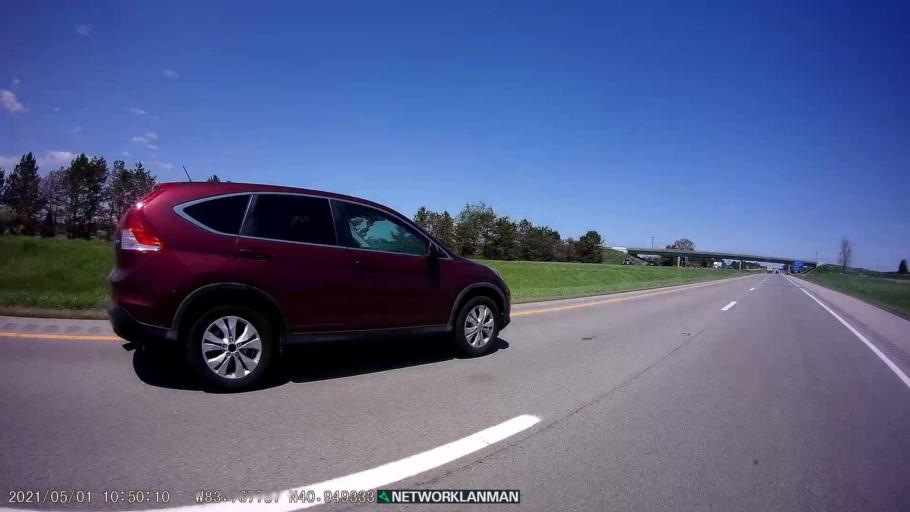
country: US
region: Ohio
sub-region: Hancock County
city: Arlington
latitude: 40.9504
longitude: -83.7684
